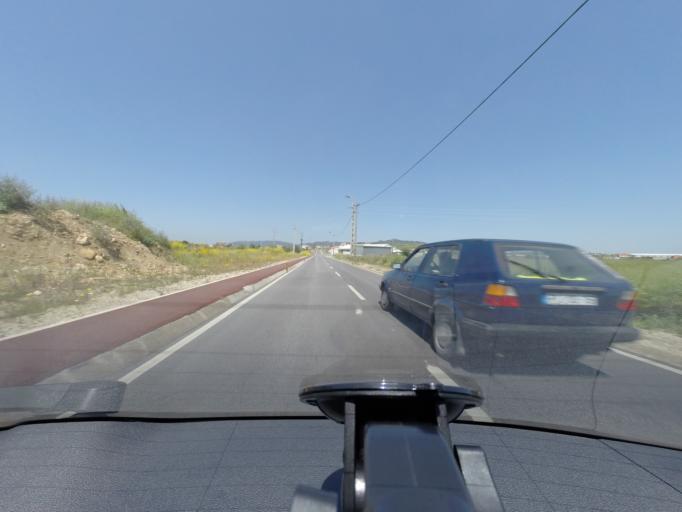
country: PT
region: Lisbon
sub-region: Cascais
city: Sao Domingos de Rana
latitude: 38.7337
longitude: -9.3510
